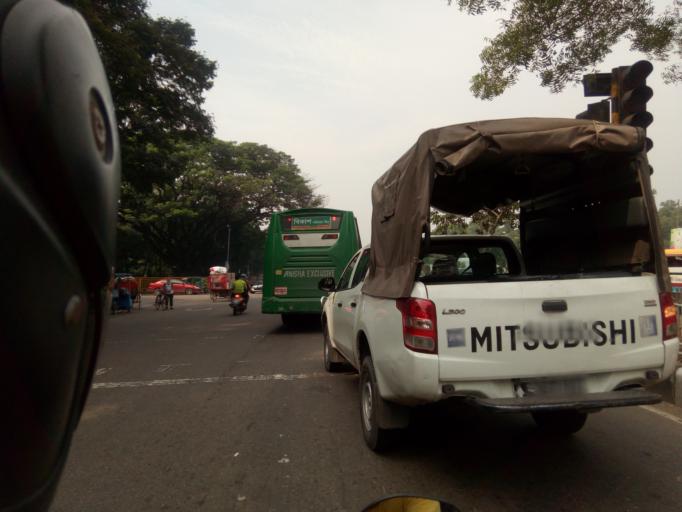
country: BD
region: Dhaka
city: Azimpur
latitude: 23.7647
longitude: 90.3833
